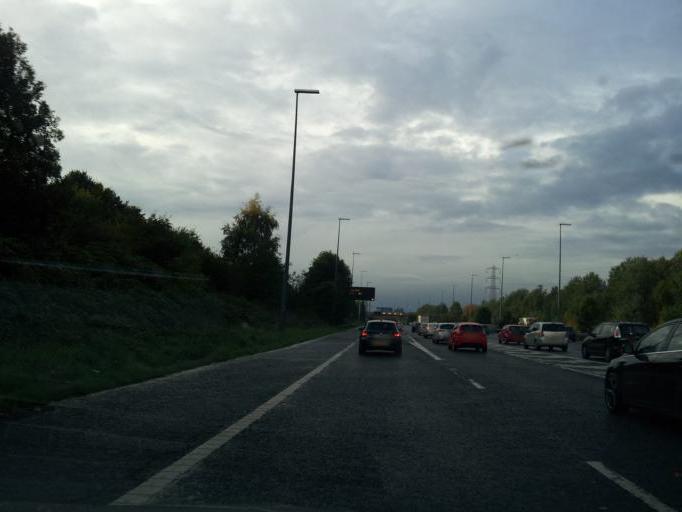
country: GB
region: England
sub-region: Manchester
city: Crumpsall
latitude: 53.5411
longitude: -2.2413
